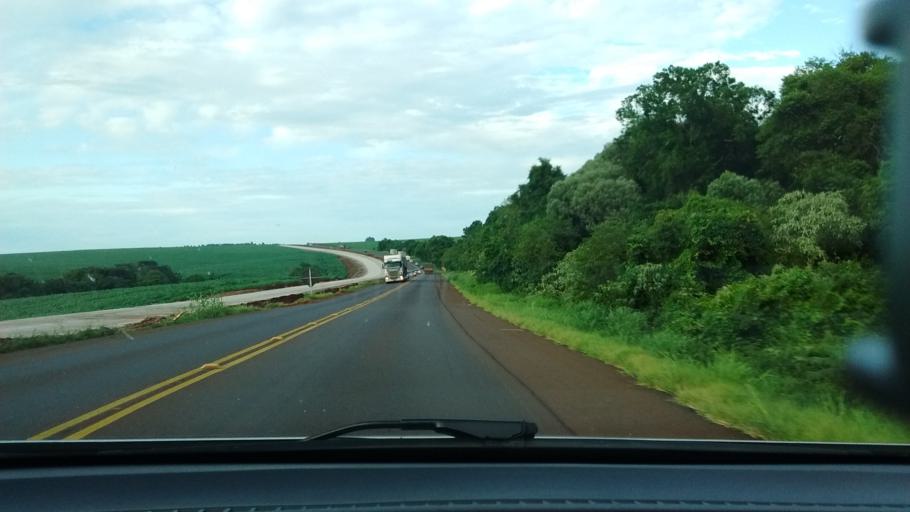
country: BR
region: Parana
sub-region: Cascavel
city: Cascavel
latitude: -25.0625
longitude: -53.5646
